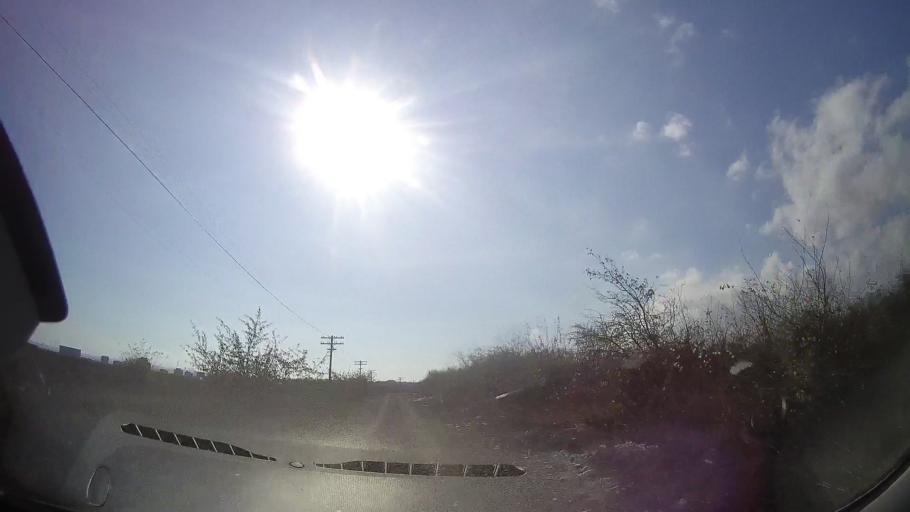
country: RO
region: Constanta
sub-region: Comuna Costinesti
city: Costinesti
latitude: 43.9705
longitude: 28.6426
